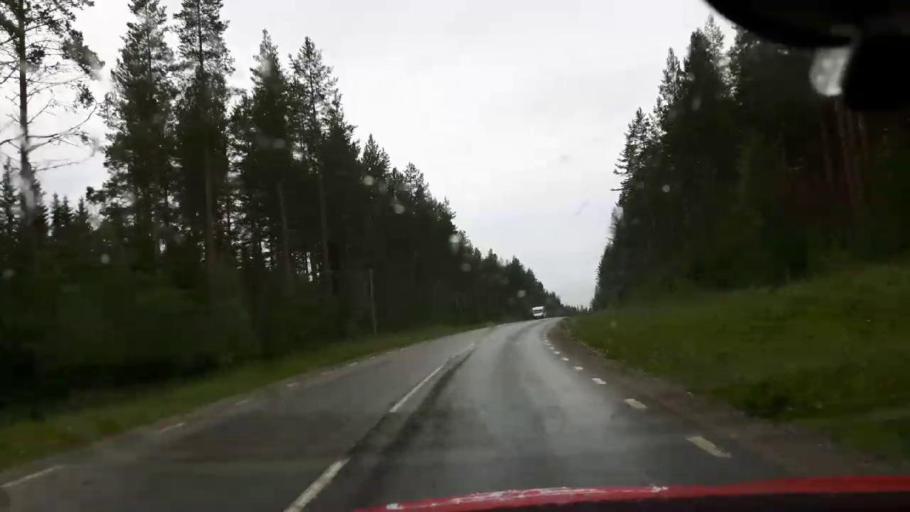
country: SE
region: Jaemtland
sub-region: OEstersunds Kommun
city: Brunflo
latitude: 62.8302
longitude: 15.0077
